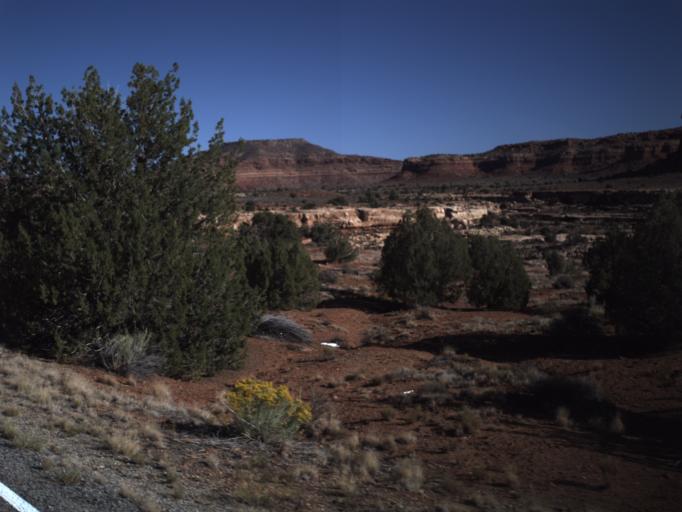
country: US
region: Utah
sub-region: San Juan County
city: Blanding
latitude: 37.7065
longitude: -110.2412
